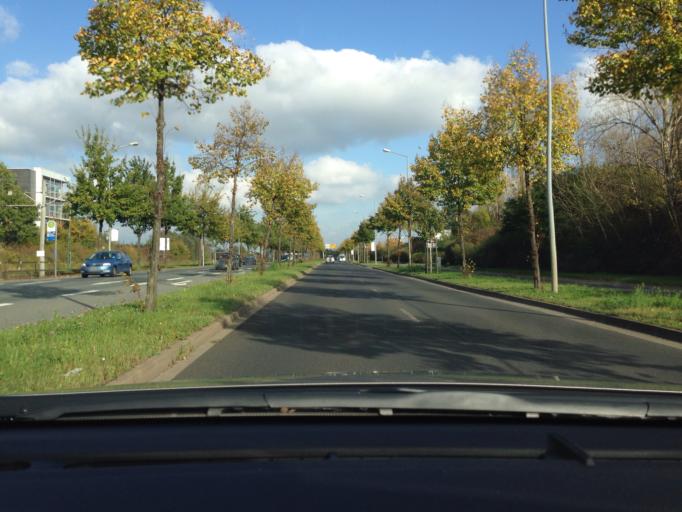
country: DE
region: Saxony
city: Taucha
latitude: 51.3614
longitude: 12.4467
